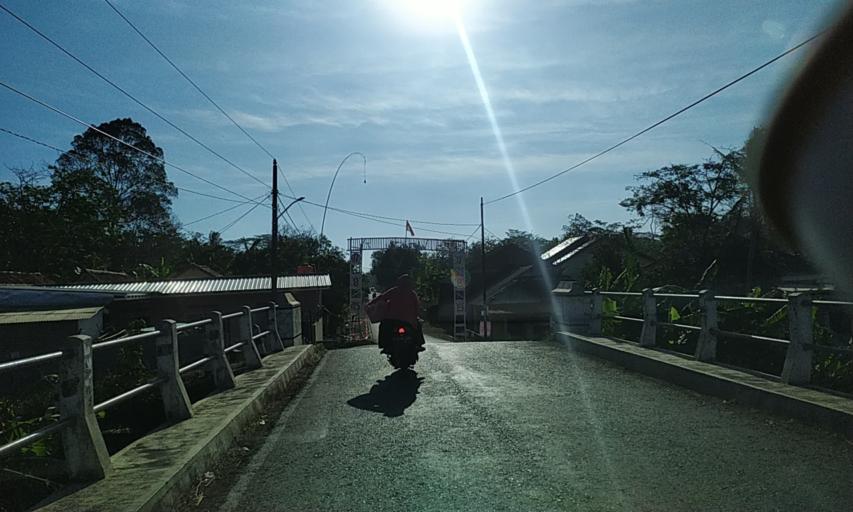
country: ID
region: Central Java
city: Kroya
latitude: -7.6267
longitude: 109.2415
